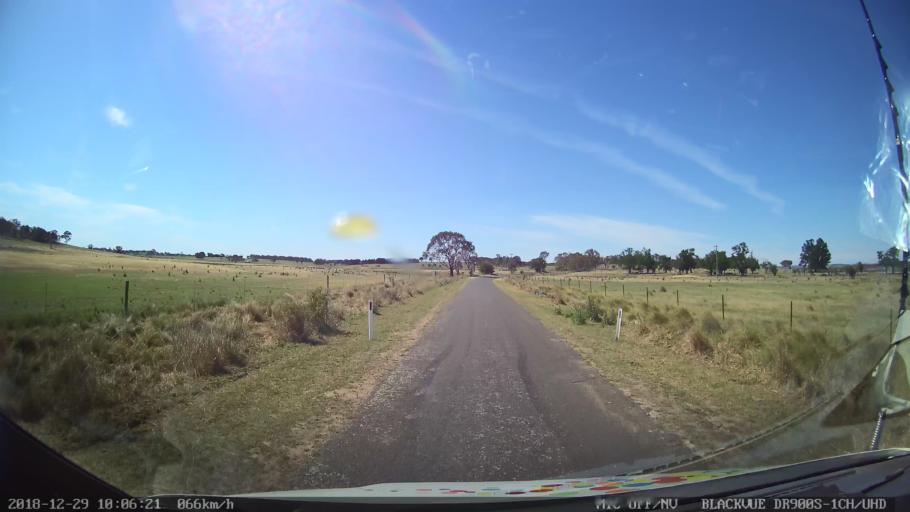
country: AU
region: New South Wales
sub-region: Yass Valley
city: Gundaroo
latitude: -34.8420
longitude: 149.4549
